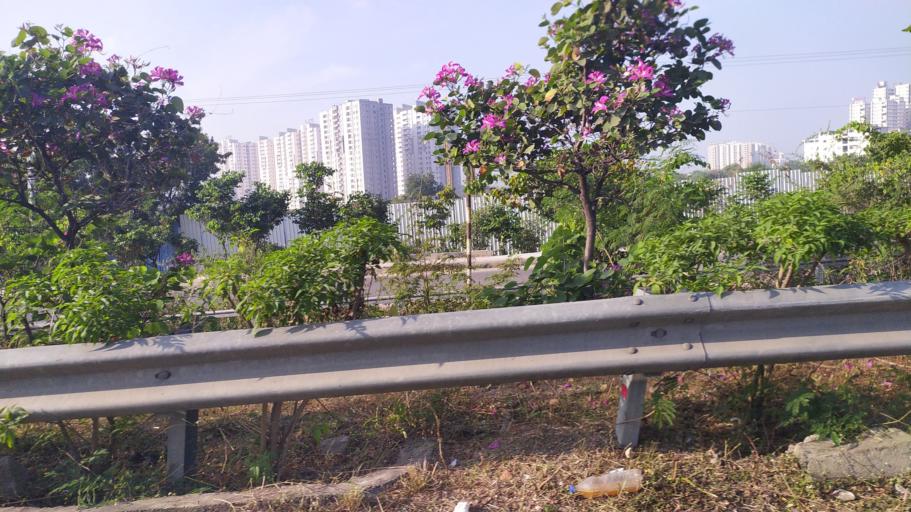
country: IN
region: Telangana
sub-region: Hyderabad
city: Hyderabad
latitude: 17.3931
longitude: 78.3511
